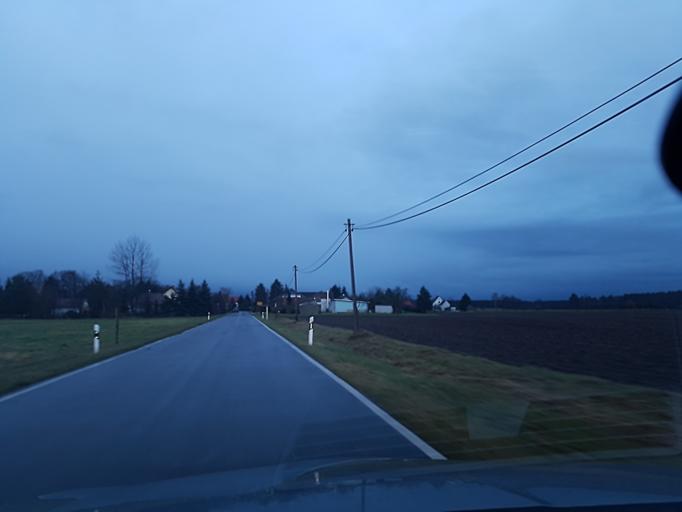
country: DE
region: Brandenburg
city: Ruckersdorf
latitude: 51.5989
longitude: 13.6056
